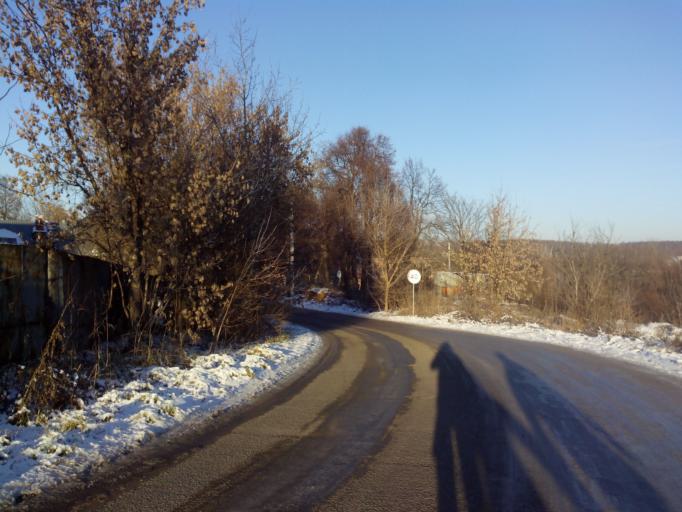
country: RU
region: Moskovskaya
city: Yakovlevskoye
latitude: 55.4977
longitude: 37.9521
